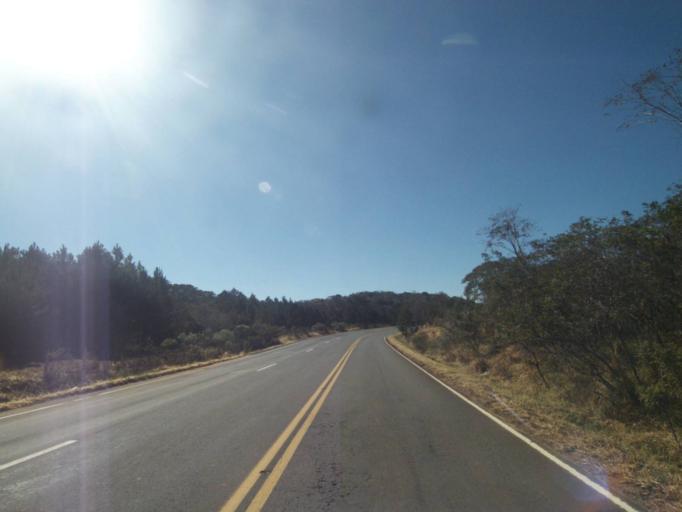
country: BR
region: Parana
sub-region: Tibagi
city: Tibagi
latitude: -24.4676
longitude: -50.4975
